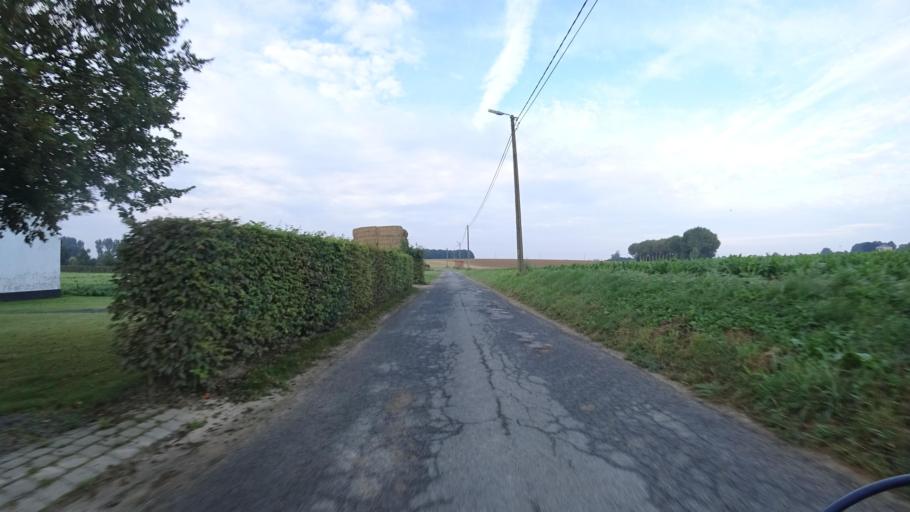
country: BE
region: Wallonia
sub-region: Province du Brabant Wallon
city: Perwez
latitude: 50.5998
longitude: 4.7573
